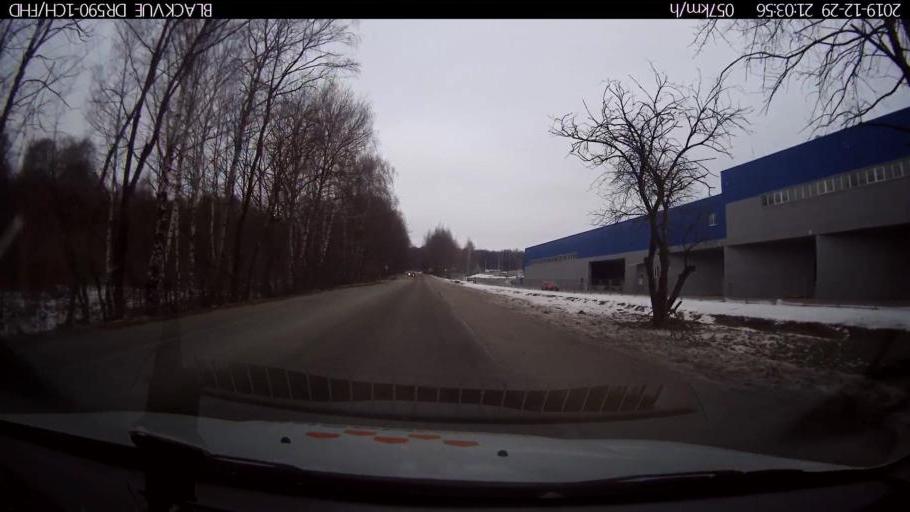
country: RU
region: Nizjnij Novgorod
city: Afonino
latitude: 56.1991
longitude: 44.0048
